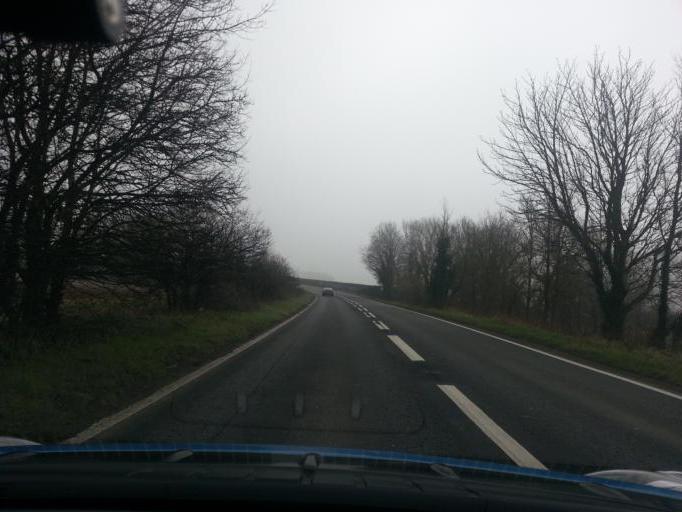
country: GB
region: England
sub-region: Oxfordshire
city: Stanford in the Vale
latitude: 51.6744
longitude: -1.4605
